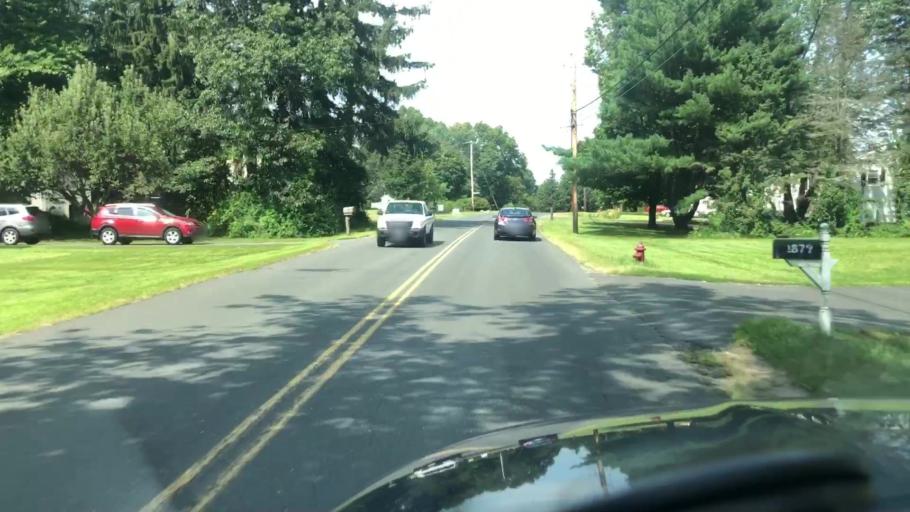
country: US
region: Massachusetts
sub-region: Hampshire County
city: Southampton
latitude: 42.1697
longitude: -72.6908
